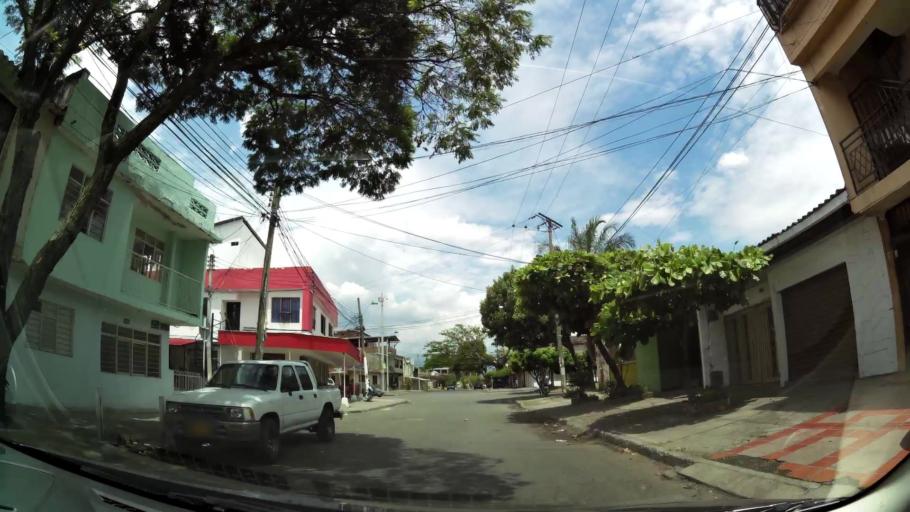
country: CO
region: Valle del Cauca
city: Cali
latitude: 3.4399
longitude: -76.5090
